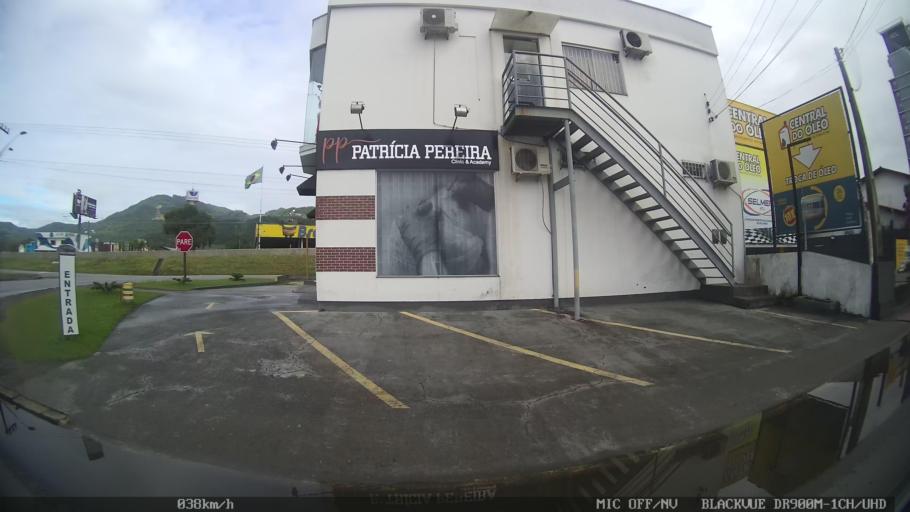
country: BR
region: Santa Catarina
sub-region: Biguacu
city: Biguacu
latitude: -27.4996
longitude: -48.6548
